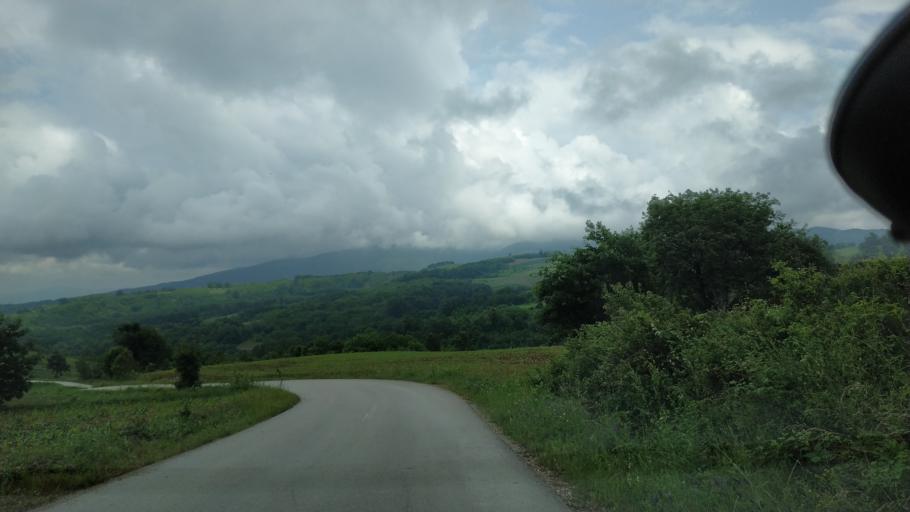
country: RS
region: Central Serbia
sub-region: Toplicki Okrug
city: Prokuplje
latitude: 43.4180
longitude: 21.5547
